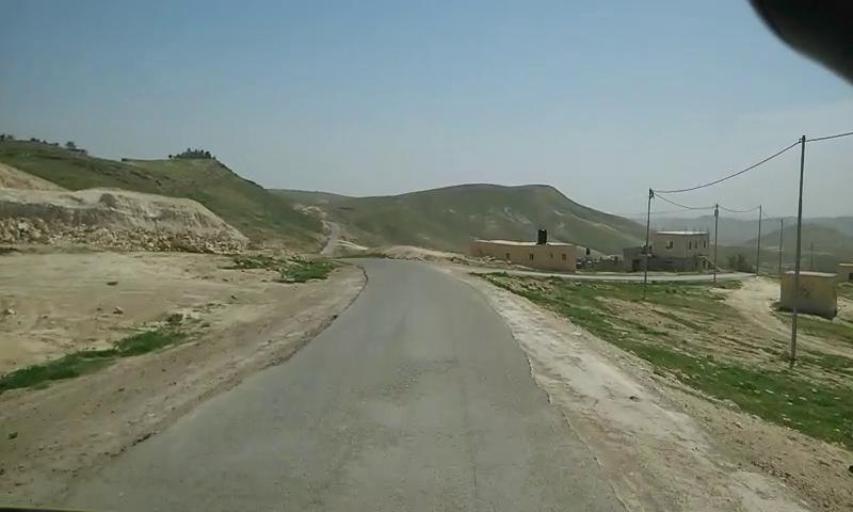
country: PS
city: `Arab ar Rashaydah
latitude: 31.5659
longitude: 35.2383
